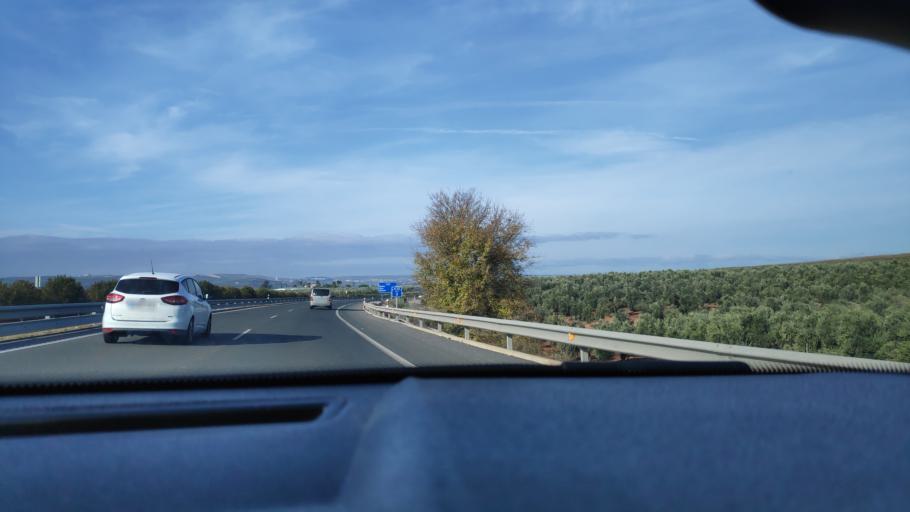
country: ES
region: Andalusia
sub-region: Provincia de Jaen
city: Linares
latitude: 38.0962
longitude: -3.7061
